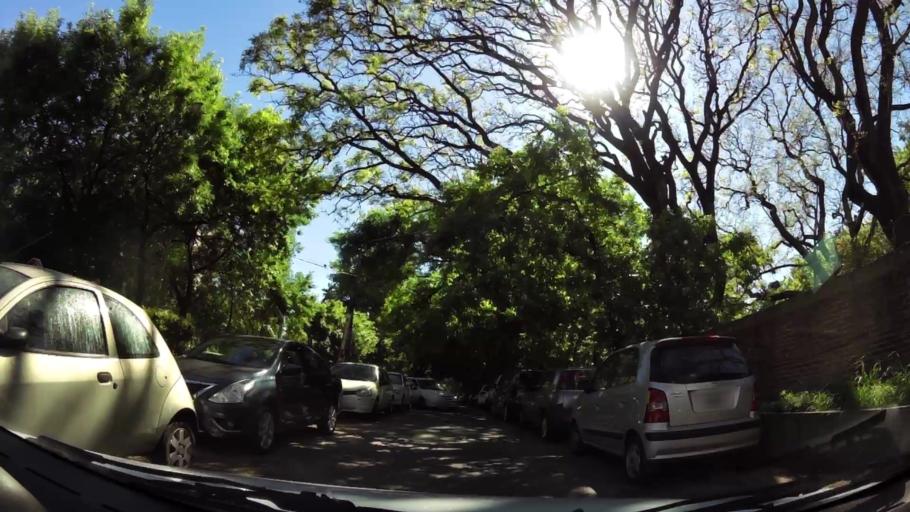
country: AR
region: Buenos Aires
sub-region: Partido de Vicente Lopez
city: Olivos
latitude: -34.5285
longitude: -58.4704
